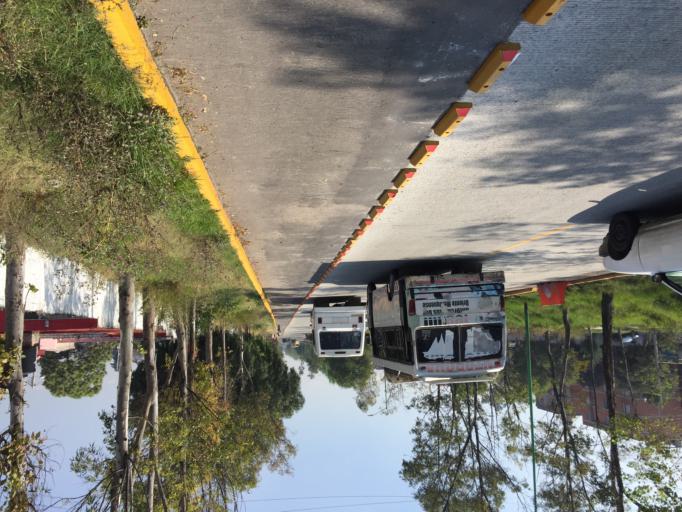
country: MX
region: Mexico
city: Cuautitlan Izcalli
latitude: 19.6417
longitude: -99.2091
